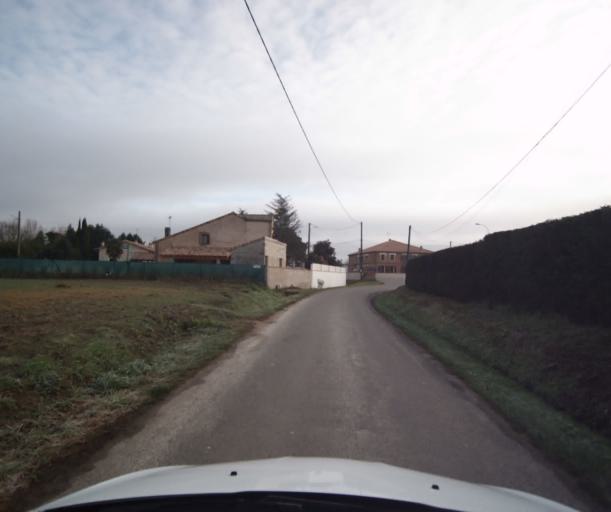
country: FR
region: Midi-Pyrenees
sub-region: Departement du Tarn-et-Garonne
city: Castelsarrasin
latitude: 44.0493
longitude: 1.0944
